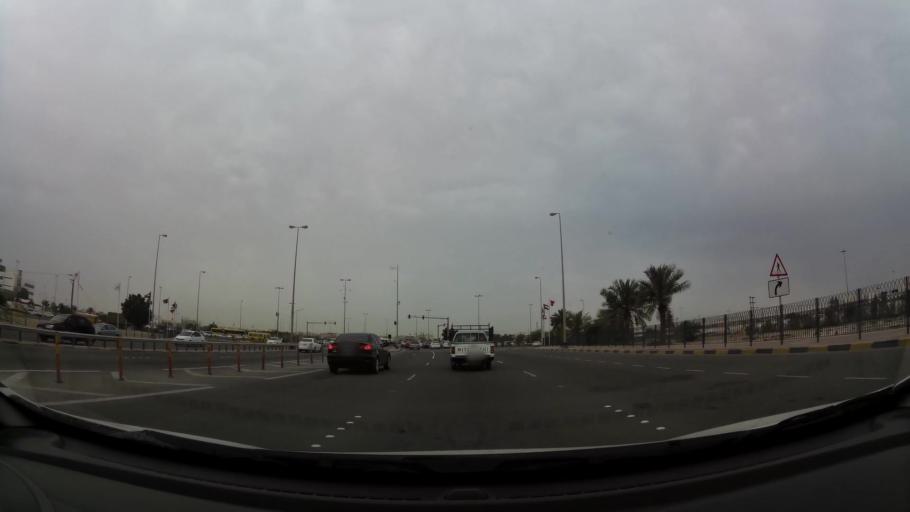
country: BH
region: Northern
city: Madinat `Isa
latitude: 26.1584
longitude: 50.5366
